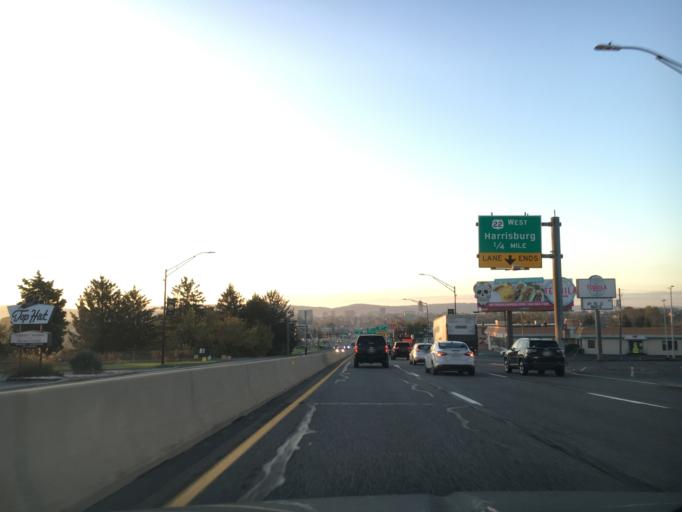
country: US
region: Pennsylvania
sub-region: Lehigh County
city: Fullerton
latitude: 40.6317
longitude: -75.4857
